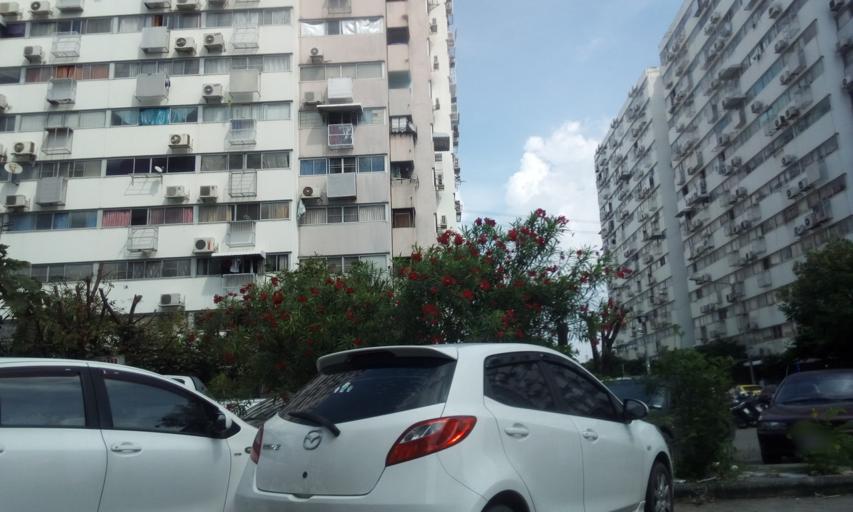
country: TH
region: Bangkok
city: Don Mueang
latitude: 13.9160
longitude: 100.5569
